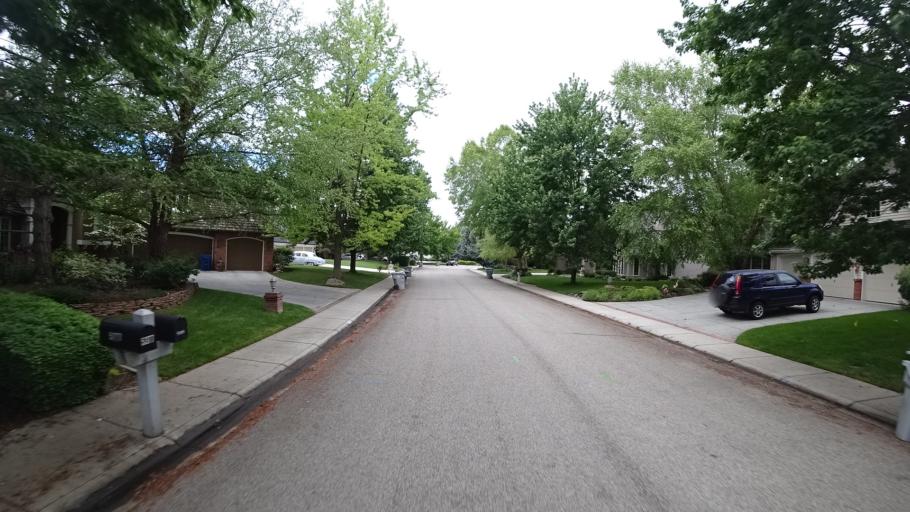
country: US
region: Idaho
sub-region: Ada County
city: Eagle
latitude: 43.6694
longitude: -116.2928
